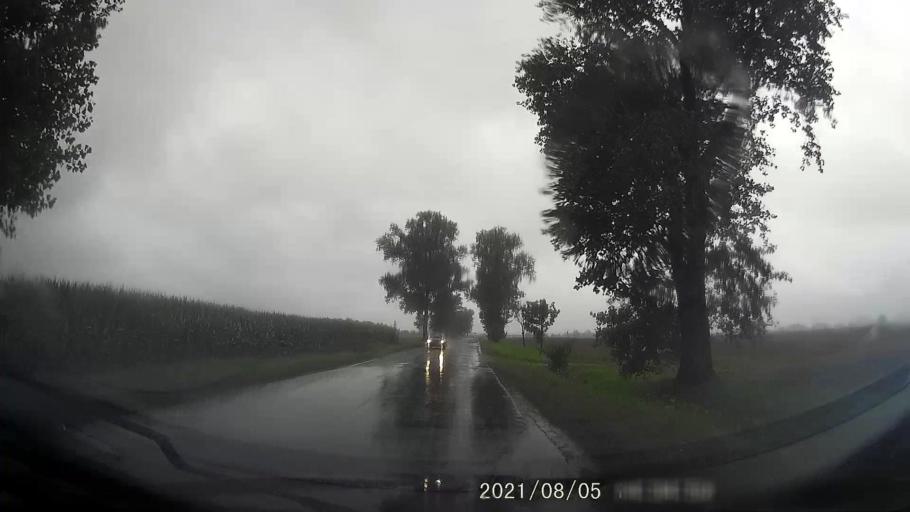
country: PL
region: Opole Voivodeship
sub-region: Powiat nyski
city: Lambinowice
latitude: 50.4673
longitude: 17.5116
